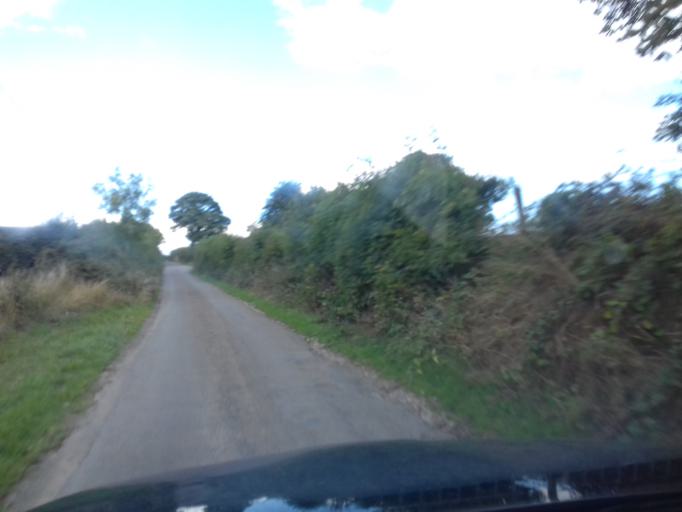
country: IE
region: Leinster
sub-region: Kilkenny
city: Graiguenamanagh
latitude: 52.5820
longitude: -7.0084
